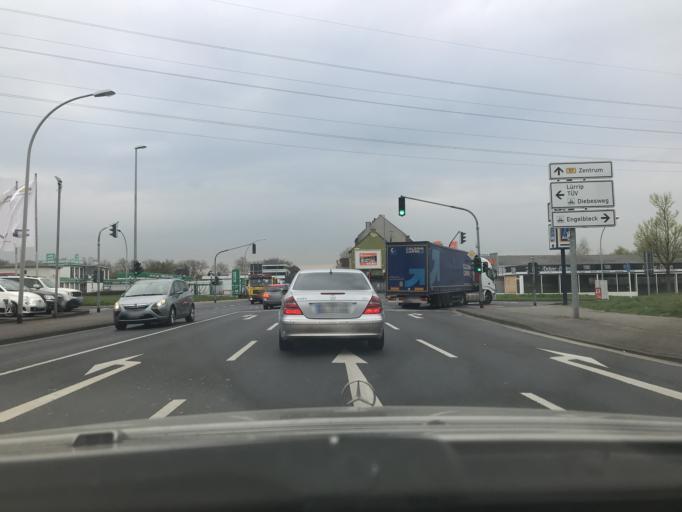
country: DE
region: North Rhine-Westphalia
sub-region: Regierungsbezirk Dusseldorf
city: Monchengladbach
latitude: 51.2110
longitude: 6.4662
